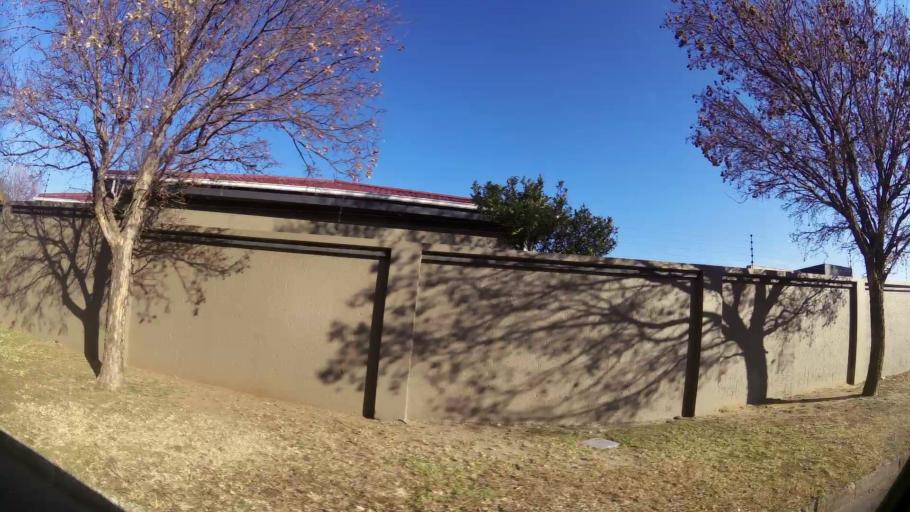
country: ZA
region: Gauteng
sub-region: Ekurhuleni Metropolitan Municipality
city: Germiston
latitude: -26.1972
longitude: 28.1233
